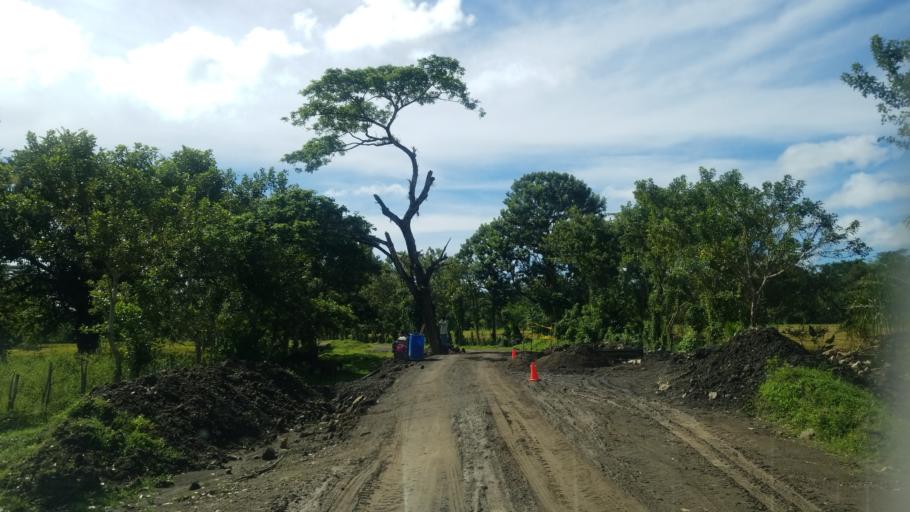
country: CR
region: Alajuela
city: San Jose
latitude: 11.0835
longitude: -85.2556
